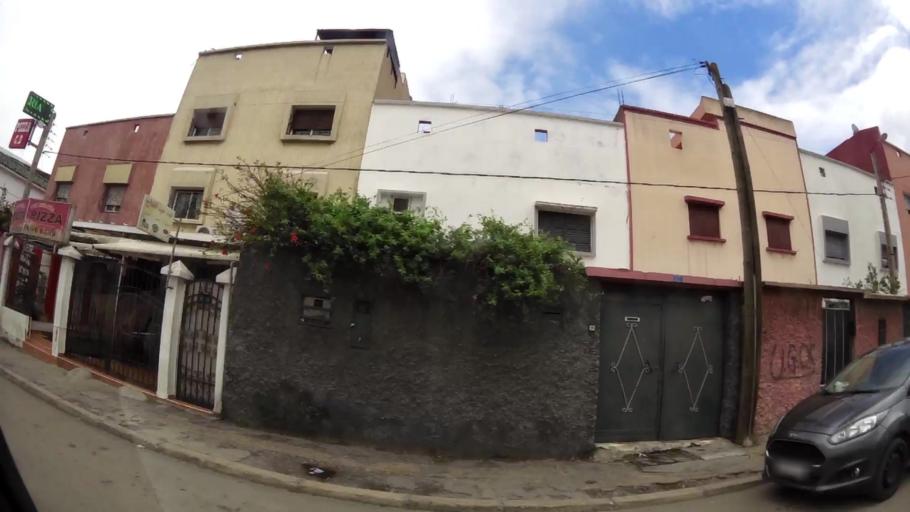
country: MA
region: Grand Casablanca
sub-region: Mediouna
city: Tit Mellil
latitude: 33.6101
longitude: -7.4971
